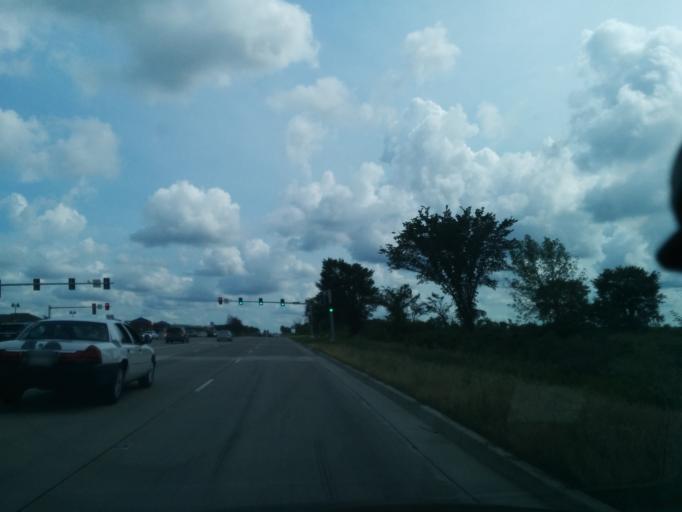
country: US
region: Illinois
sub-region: Cook County
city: Orland Hills
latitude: 41.5803
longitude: -87.8522
